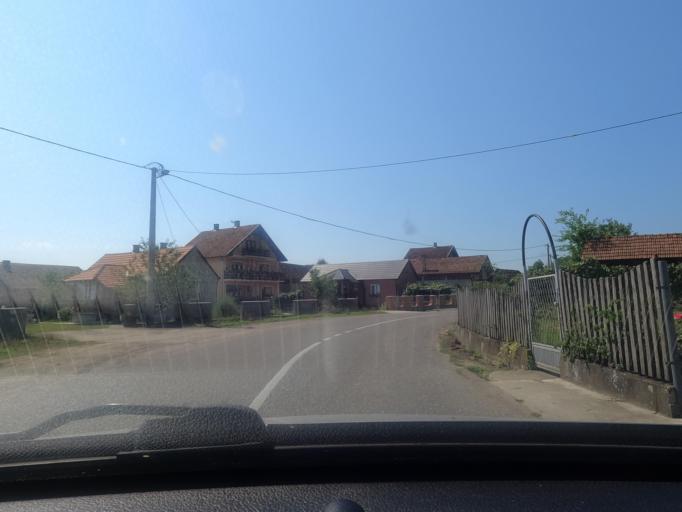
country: RS
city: Kozjak
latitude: 44.5571
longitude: 19.3177
